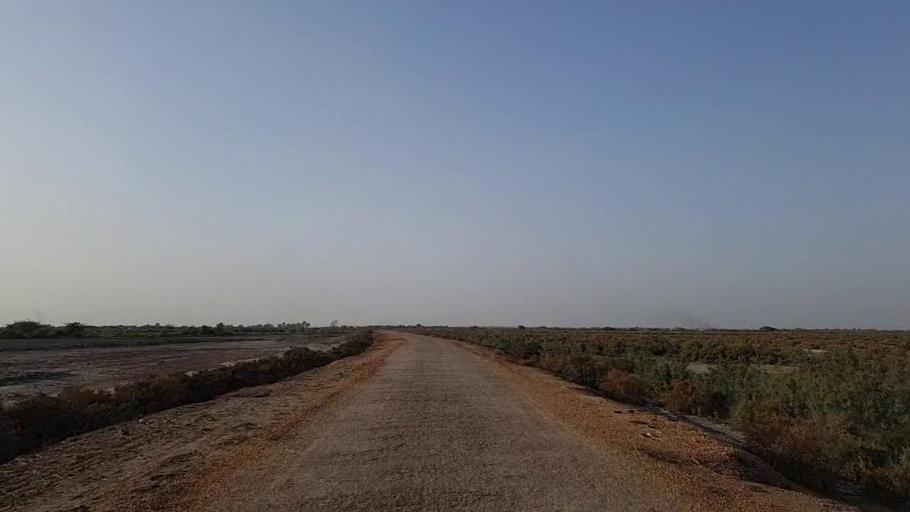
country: PK
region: Sindh
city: Jati
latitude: 24.3610
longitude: 68.1462
